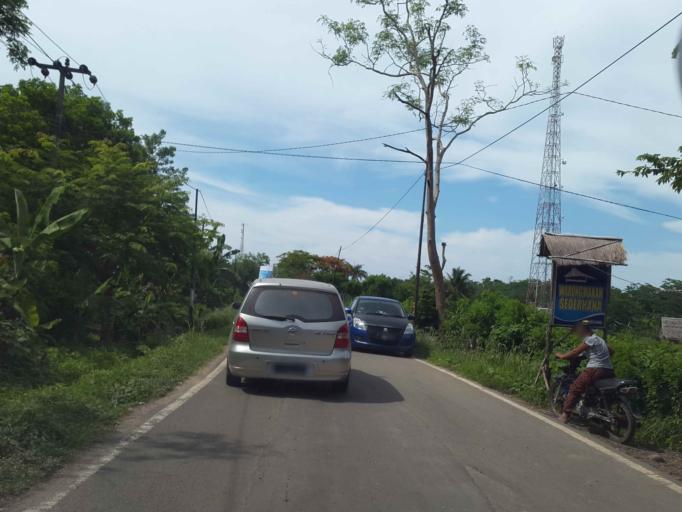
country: ID
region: Banten
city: Citeureup
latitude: -6.5041
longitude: 105.6692
